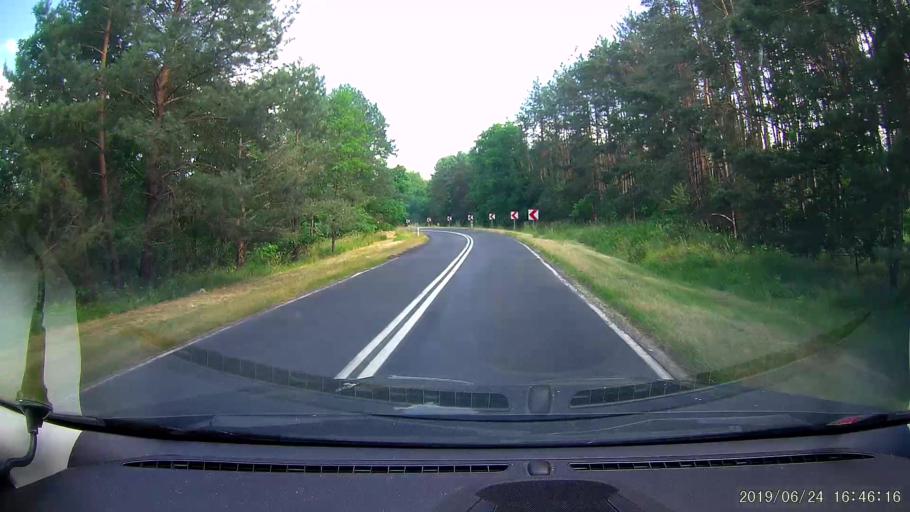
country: PL
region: Lublin Voivodeship
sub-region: Powiat tomaszowski
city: Laszczow
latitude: 50.5269
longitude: 23.6757
